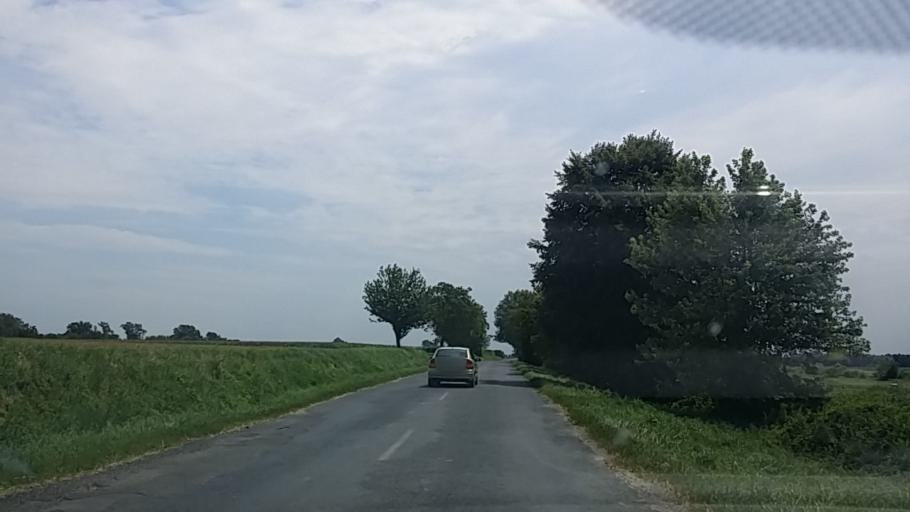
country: HR
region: Medimurska
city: Kotoriba
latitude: 46.3945
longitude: 16.8094
